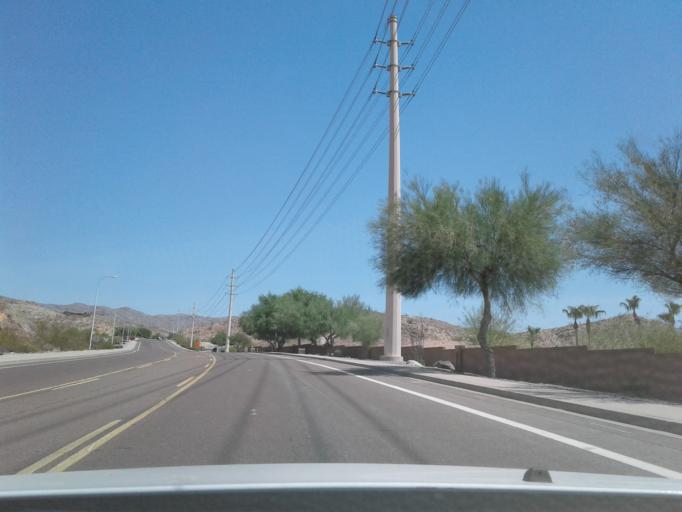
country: US
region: Arizona
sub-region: Maricopa County
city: Guadalupe
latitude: 33.2932
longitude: -112.0319
